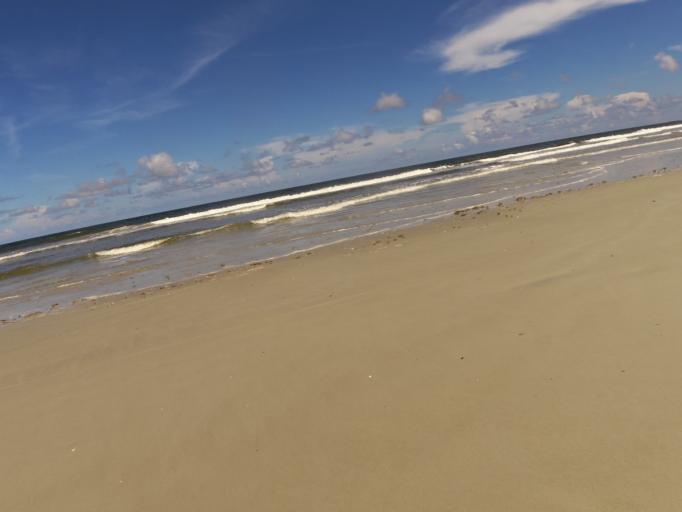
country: US
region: Florida
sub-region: Duval County
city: Atlantic Beach
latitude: 30.4732
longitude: -81.4127
